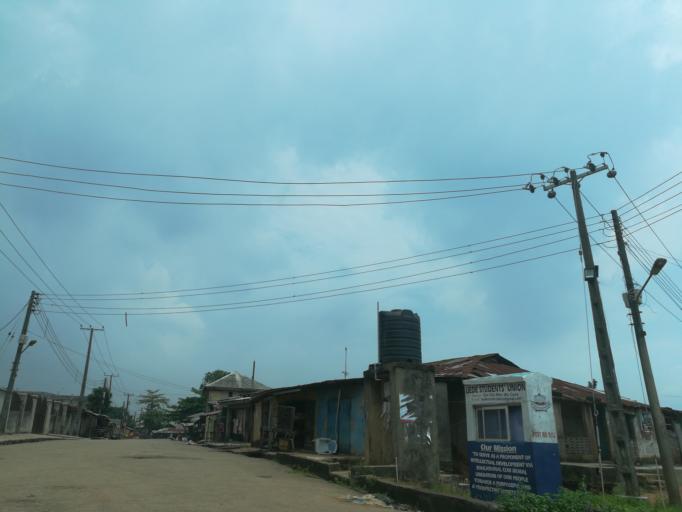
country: NG
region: Lagos
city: Ikorodu
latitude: 6.5648
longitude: 3.5915
